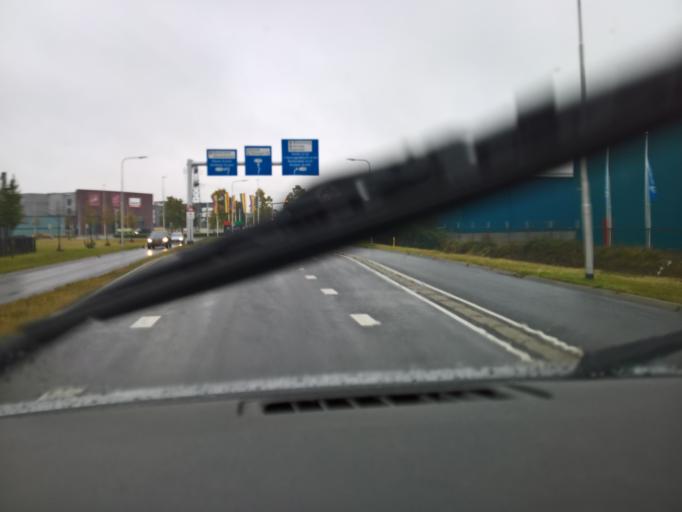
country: NL
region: Gelderland
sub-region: Gemeente Nijmegen
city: Nijmegen
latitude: 51.8511
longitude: 5.8310
